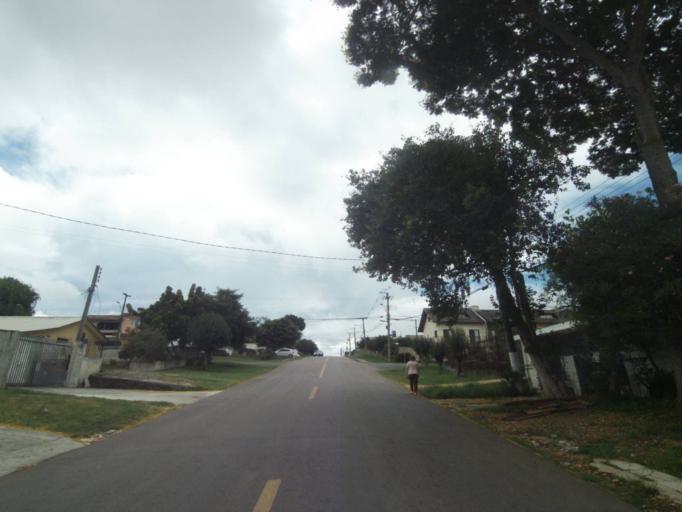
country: BR
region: Parana
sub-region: Curitiba
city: Curitiba
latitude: -25.4845
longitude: -49.2802
